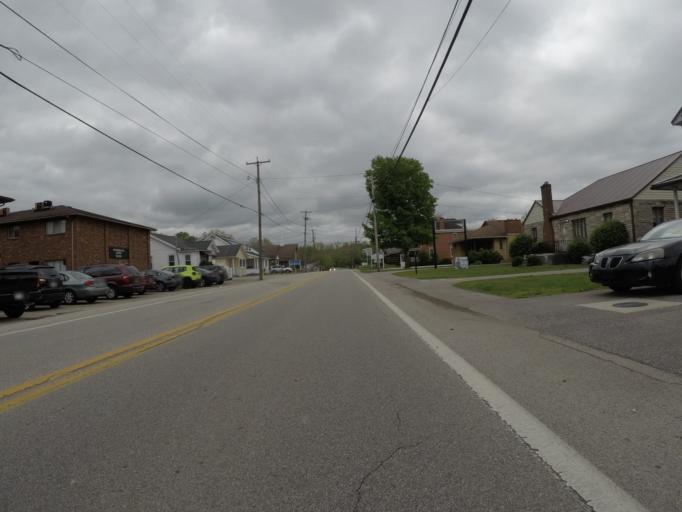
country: US
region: West Virginia
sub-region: Cabell County
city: Barboursville
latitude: 38.4138
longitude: -82.2990
